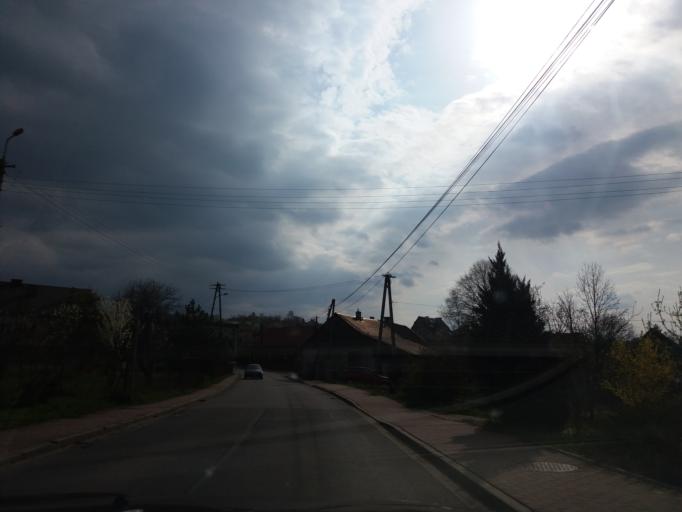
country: PL
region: Lesser Poland Voivodeship
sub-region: Powiat myslenicki
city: Dobczyce
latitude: 49.8787
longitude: 20.1017
